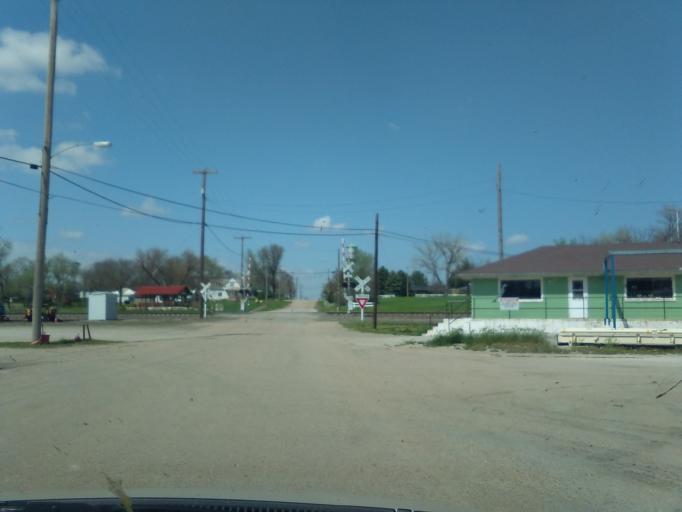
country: US
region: Nebraska
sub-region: Thayer County
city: Hebron
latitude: 40.2522
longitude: -97.5579
